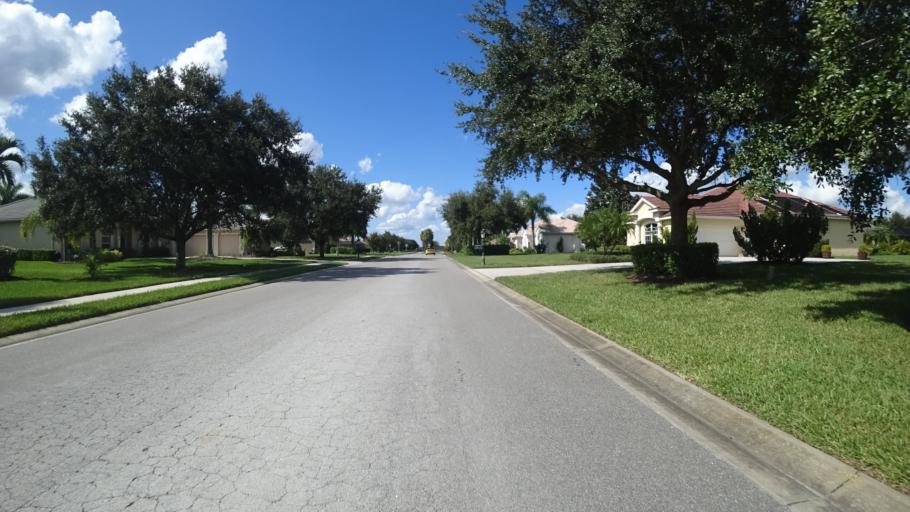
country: US
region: Florida
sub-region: Manatee County
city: Ellenton
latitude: 27.5032
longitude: -82.3714
